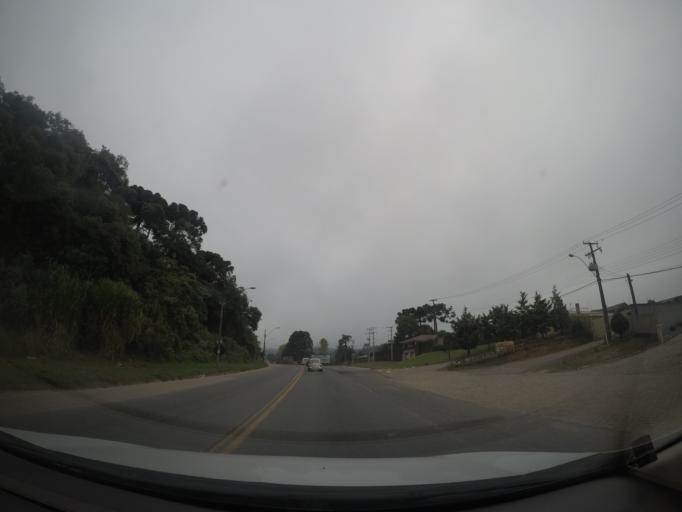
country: BR
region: Parana
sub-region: Almirante Tamandare
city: Almirante Tamandare
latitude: -25.3393
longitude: -49.2835
